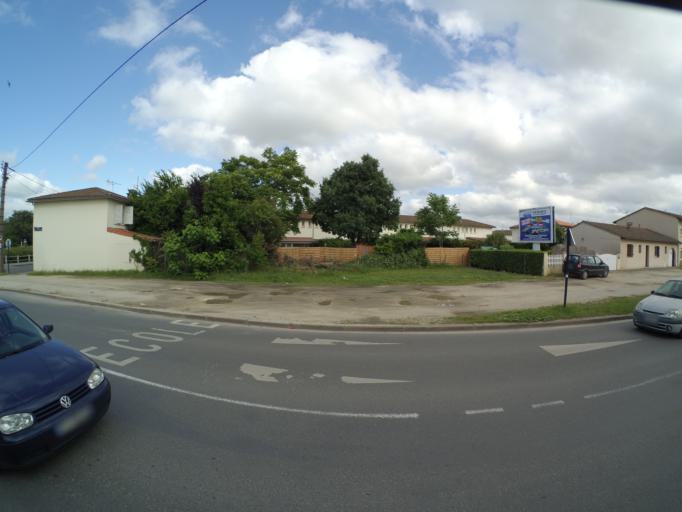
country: FR
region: Aquitaine
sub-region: Departement de la Gironde
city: Lormont
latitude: 44.8744
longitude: -0.5538
